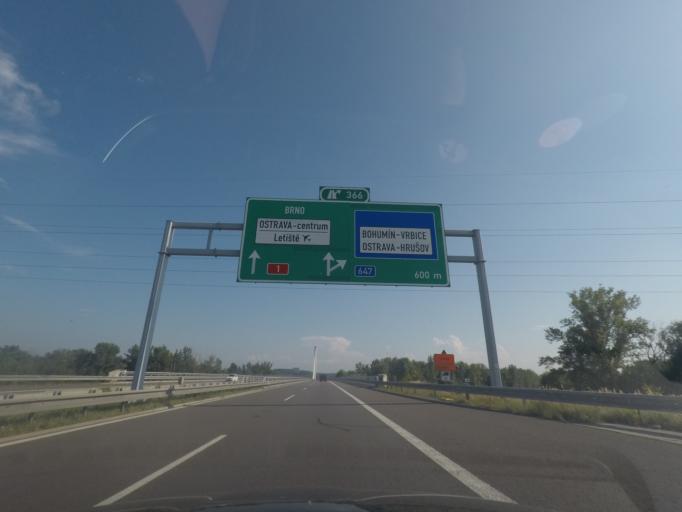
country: PL
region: Silesian Voivodeship
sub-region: Powiat raciborski
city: Chalupki
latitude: 49.8914
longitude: 18.3037
